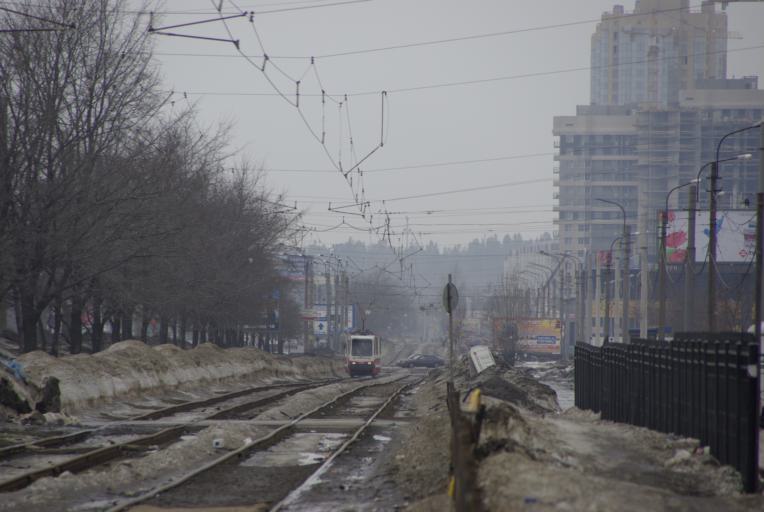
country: RU
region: St.-Petersburg
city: Ozerki
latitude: 60.0371
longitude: 30.3198
